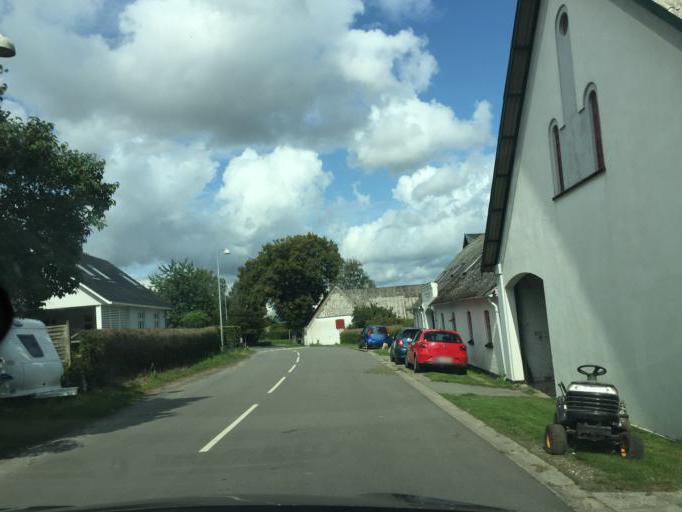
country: DK
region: South Denmark
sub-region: Odense Kommune
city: Stige
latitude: 55.4620
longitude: 10.3758
